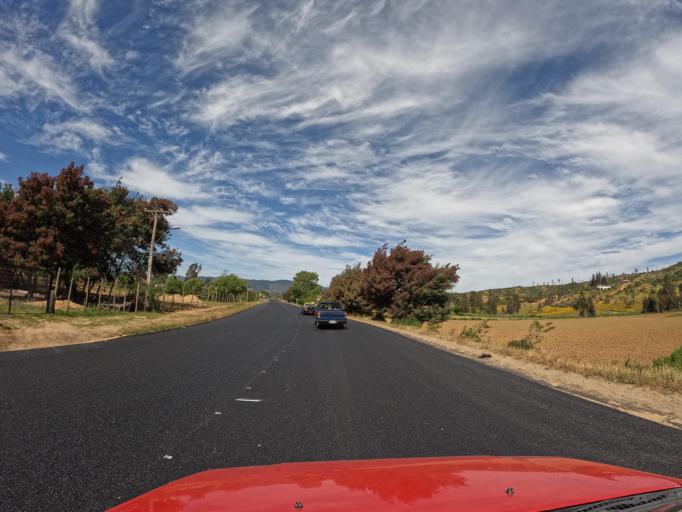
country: CL
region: Maule
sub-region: Provincia de Talca
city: Constitucion
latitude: -35.0993
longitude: -72.0034
